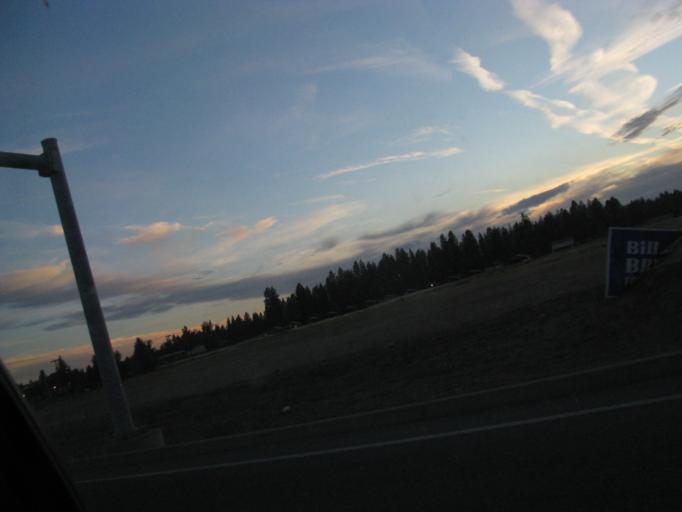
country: US
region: Washington
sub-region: Spokane County
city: Mead
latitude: 47.7881
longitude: -117.3531
